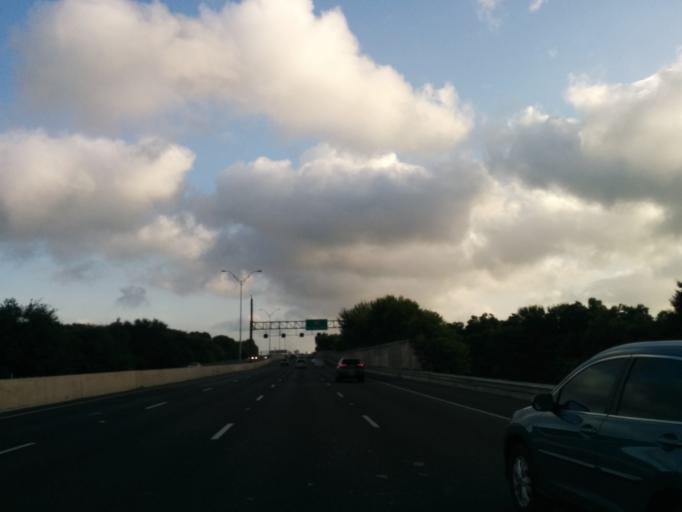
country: US
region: Texas
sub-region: Bexar County
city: Olmos Park
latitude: 29.4787
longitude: -98.4811
